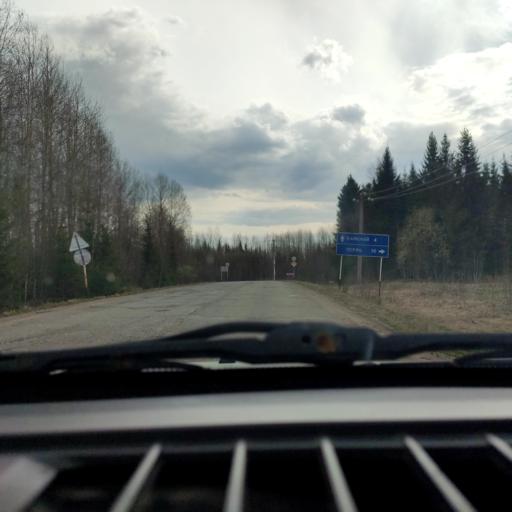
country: RU
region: Perm
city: Polazna
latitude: 58.3398
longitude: 56.1782
